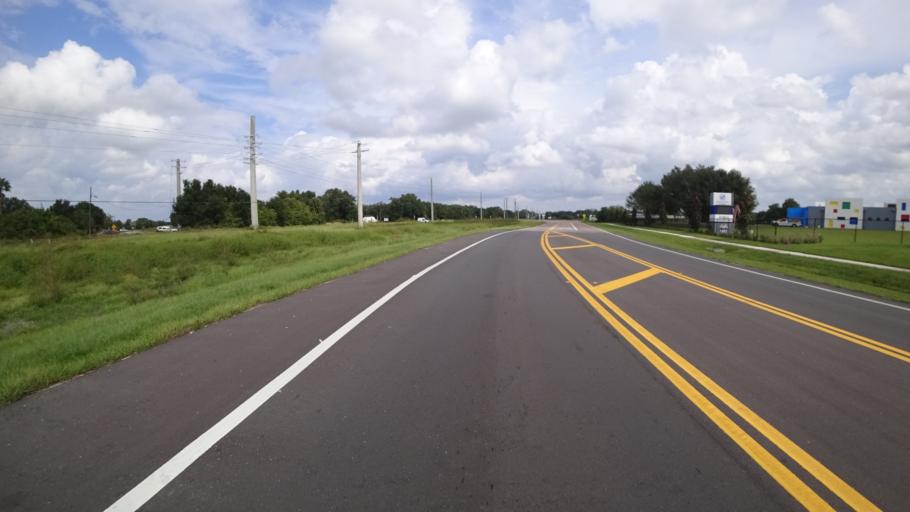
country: US
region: Florida
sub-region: Manatee County
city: Ellenton
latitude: 27.5708
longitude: -82.4781
